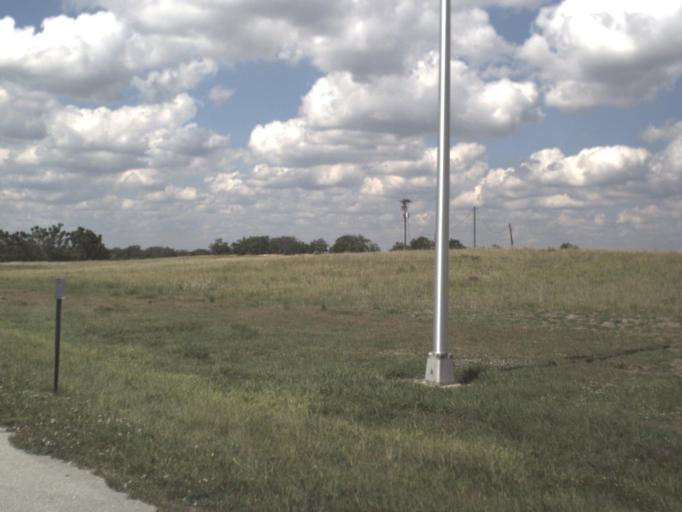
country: US
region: Florida
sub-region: Highlands County
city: Sebring
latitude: 27.4291
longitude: -81.4193
